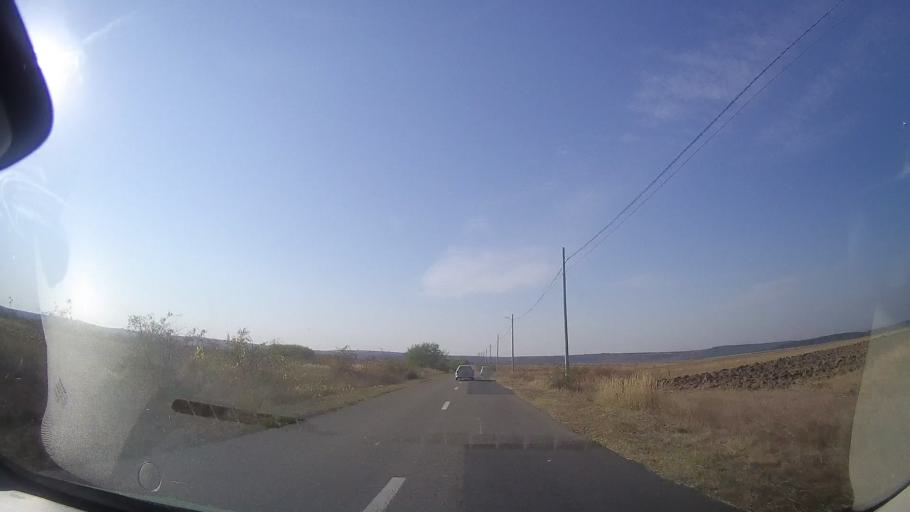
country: RO
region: Timis
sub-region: Oras Recas
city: Recas
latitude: 45.8727
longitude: 21.5173
